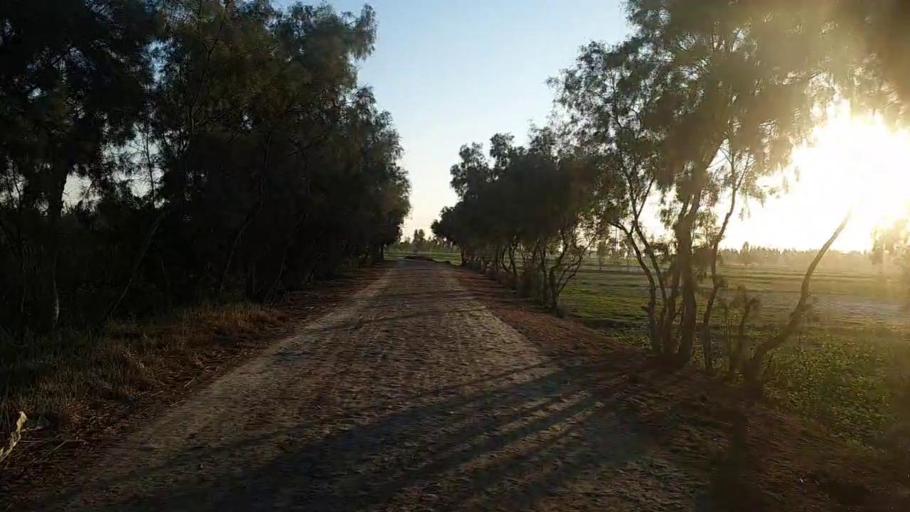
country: PK
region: Sindh
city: Khairpur
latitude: 27.9152
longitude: 69.6893
